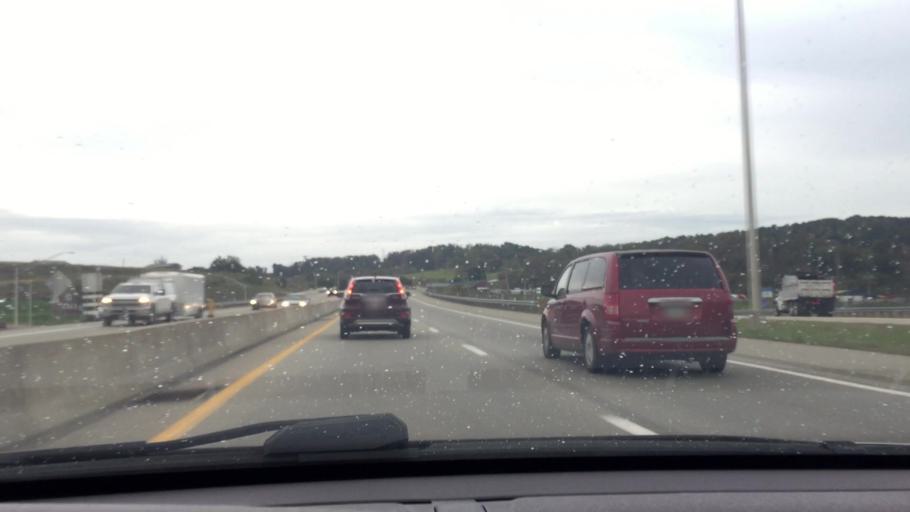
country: US
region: Pennsylvania
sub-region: Washington County
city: East Washington
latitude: 40.1561
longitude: -80.1345
